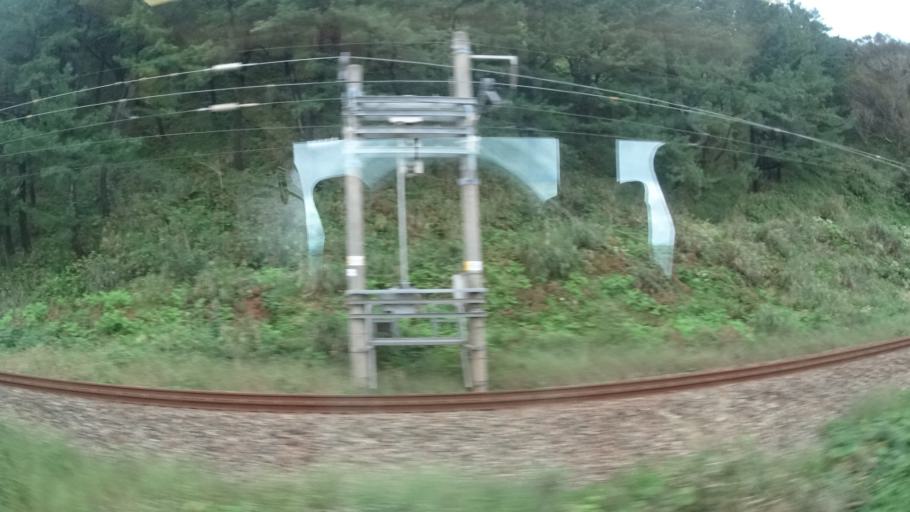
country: JP
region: Niigata
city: Murakami
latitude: 38.3627
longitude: 139.4526
